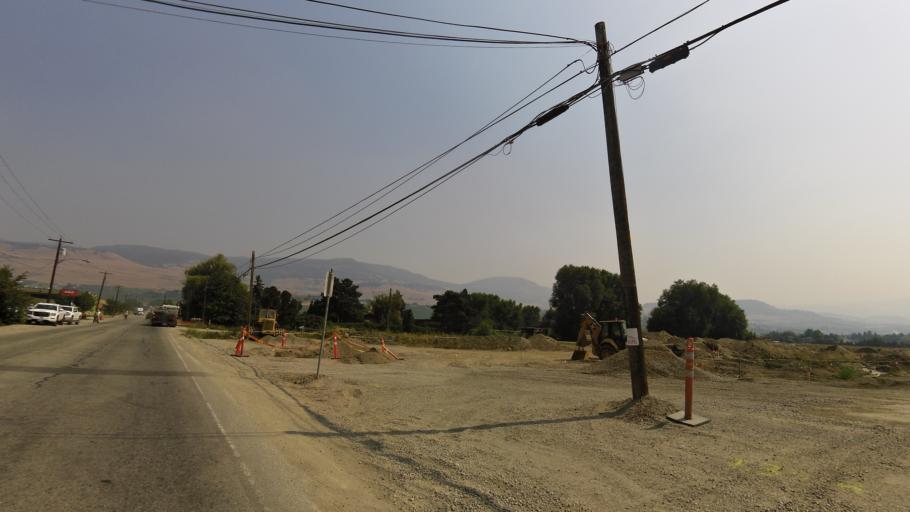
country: CA
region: British Columbia
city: Kelowna
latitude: 49.9181
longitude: -119.3840
